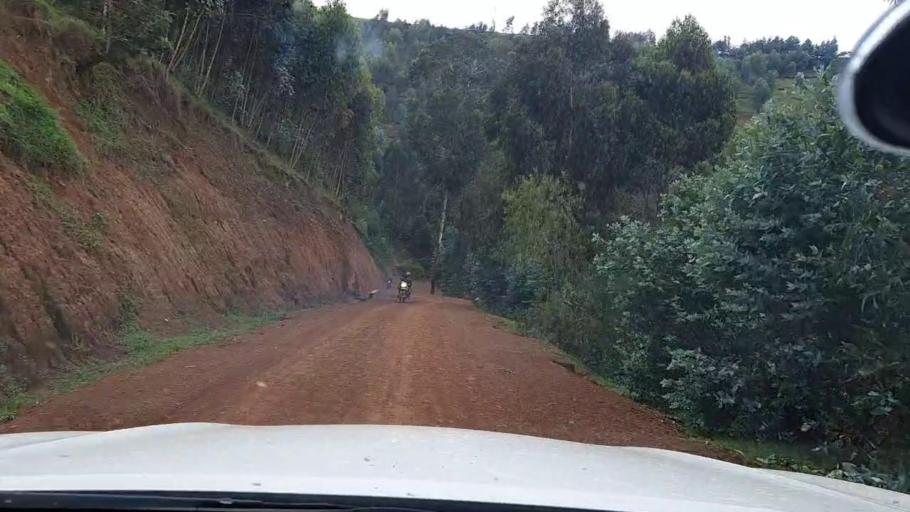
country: RW
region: Western Province
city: Kibuye
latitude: -2.1708
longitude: 29.4361
